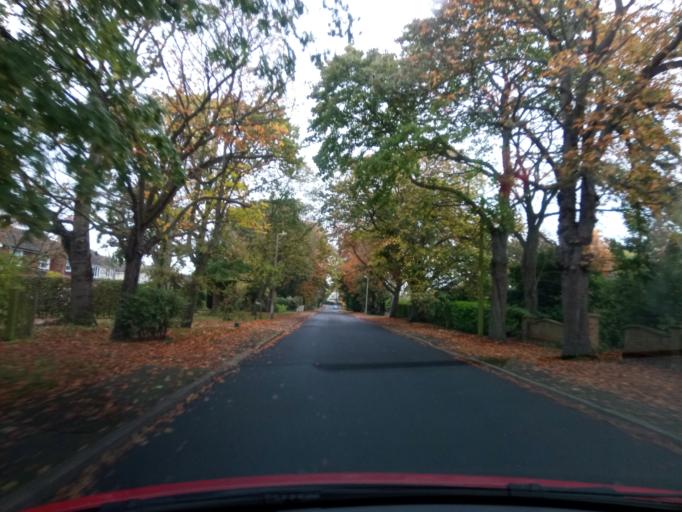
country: GB
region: England
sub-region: Essex
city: West Mersea
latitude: 51.7794
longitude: 0.9271
